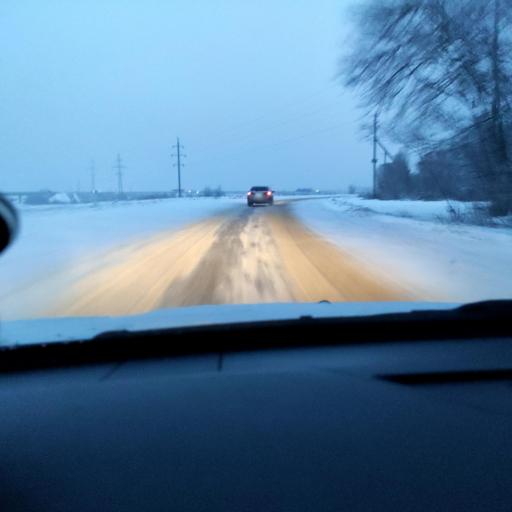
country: RU
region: Samara
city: Smyshlyayevka
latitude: 53.2602
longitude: 50.4673
